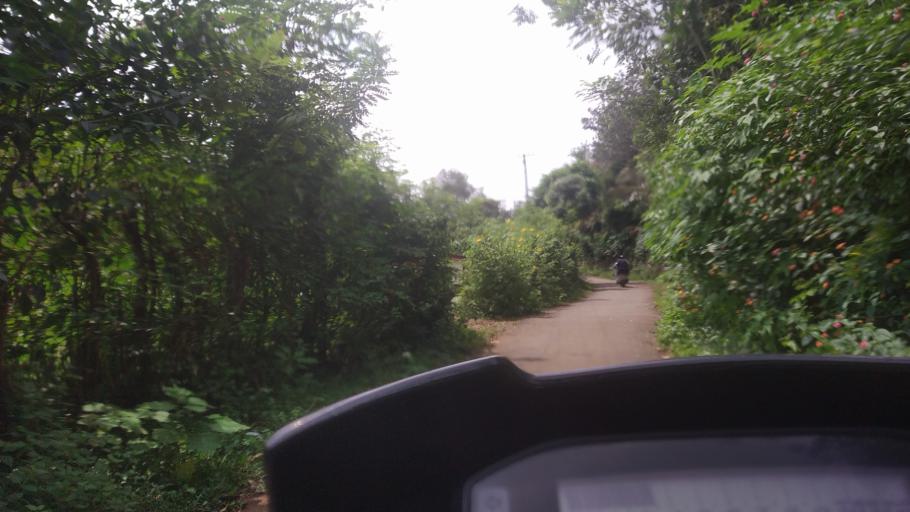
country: IN
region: Tamil Nadu
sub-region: Theni
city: Gudalur
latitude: 9.5780
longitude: 77.0760
